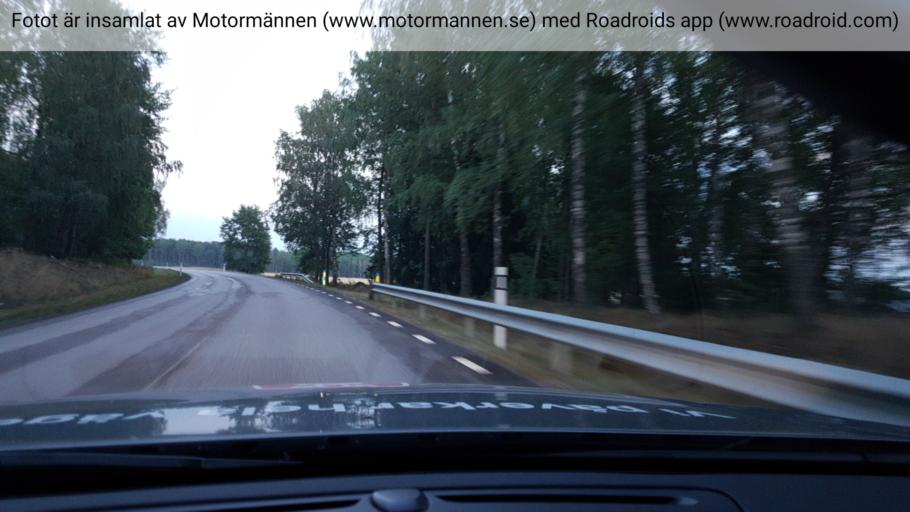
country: SE
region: Vaestmanland
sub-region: Sala Kommun
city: Sala
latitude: 59.8275
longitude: 16.7268
